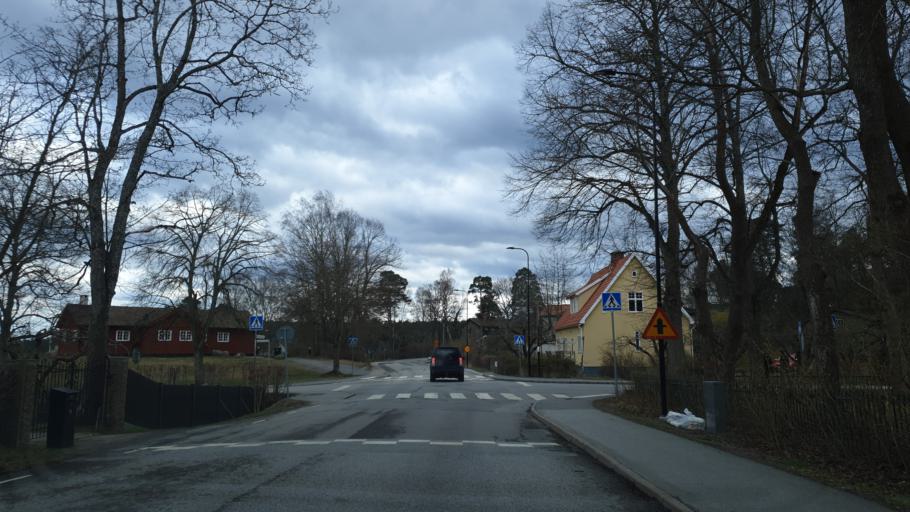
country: SE
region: Stockholm
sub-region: Nacka Kommun
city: Nacka
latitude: 59.3033
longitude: 18.2017
